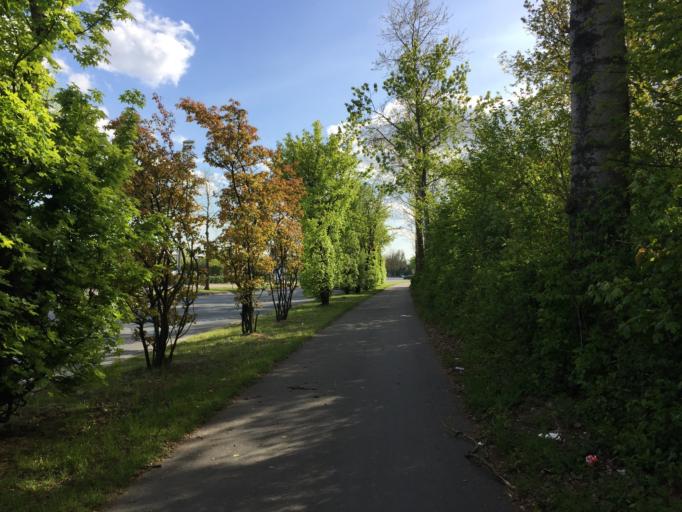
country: DE
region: North Rhine-Westphalia
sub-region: Regierungsbezirk Munster
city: Muenster
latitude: 51.9383
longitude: 7.6443
